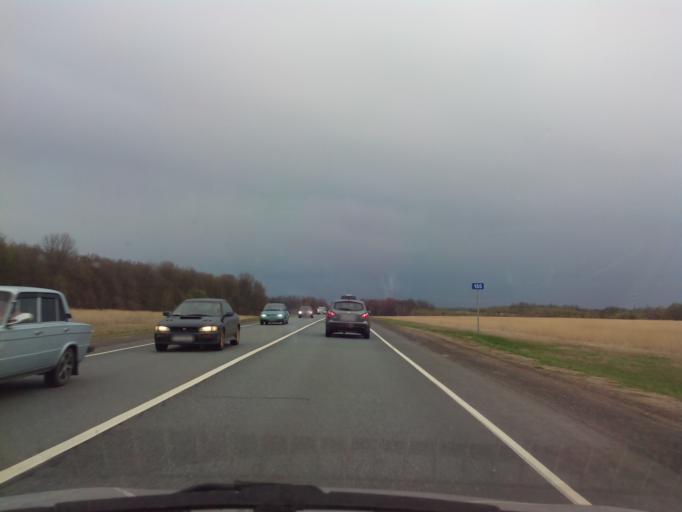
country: RU
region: Moskovskaya
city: Uzunovo
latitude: 54.5524
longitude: 38.4636
